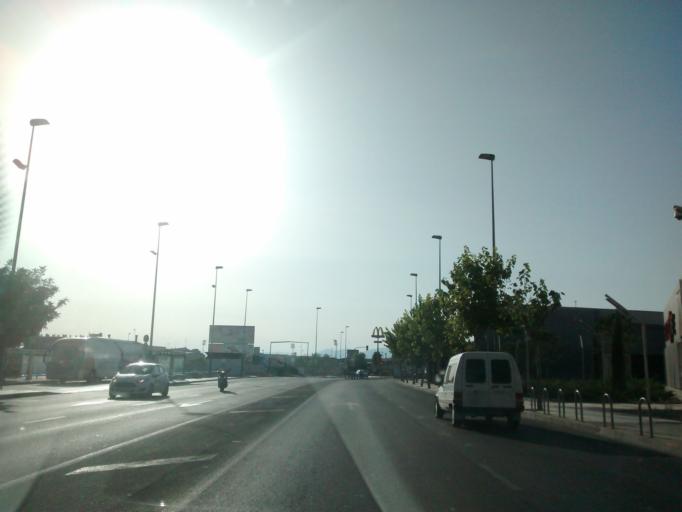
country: ES
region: Valencia
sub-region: Provincia de Alicante
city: Santa Pola
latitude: 38.1964
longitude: -0.5609
